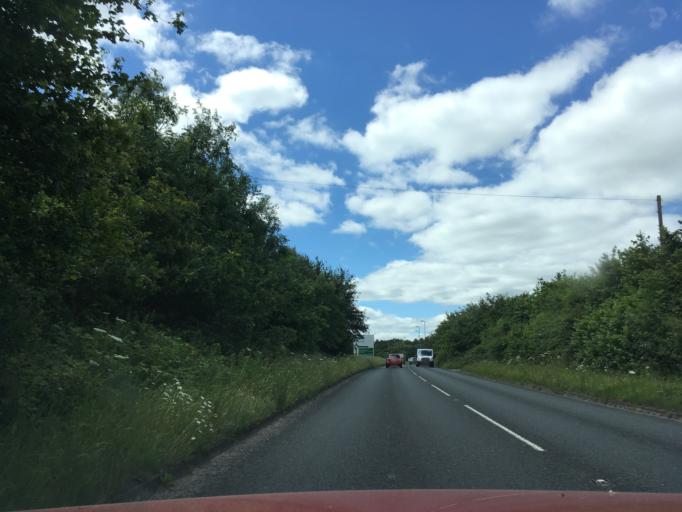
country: GB
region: England
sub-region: Hampshire
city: Highclere
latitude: 51.3653
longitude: -1.3534
